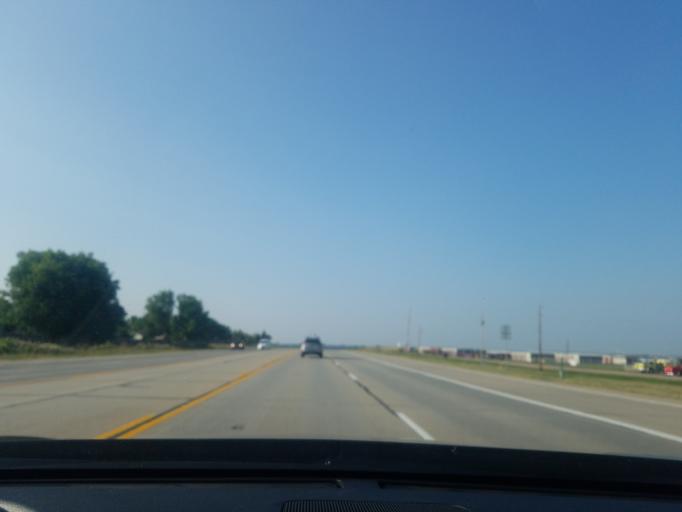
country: US
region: Colorado
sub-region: Larimer County
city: Campion
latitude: 40.3649
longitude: -105.0732
